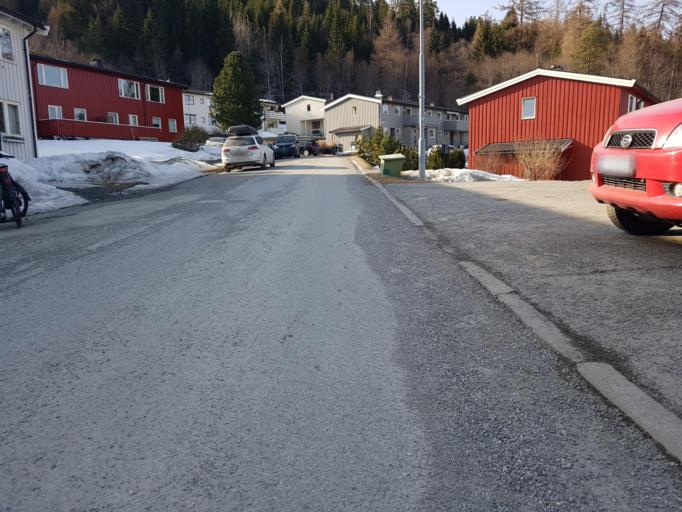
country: NO
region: Sor-Trondelag
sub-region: Trondheim
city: Trondheim
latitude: 63.4295
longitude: 10.3460
